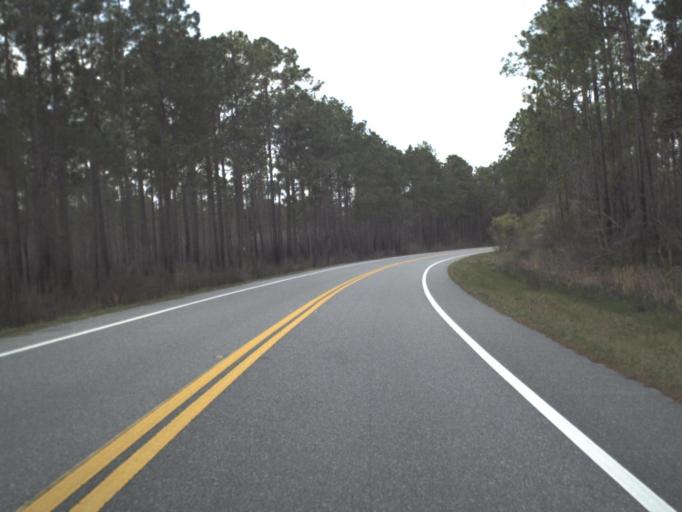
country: US
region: Florida
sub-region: Franklin County
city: Apalachicola
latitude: 29.8484
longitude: -84.9713
